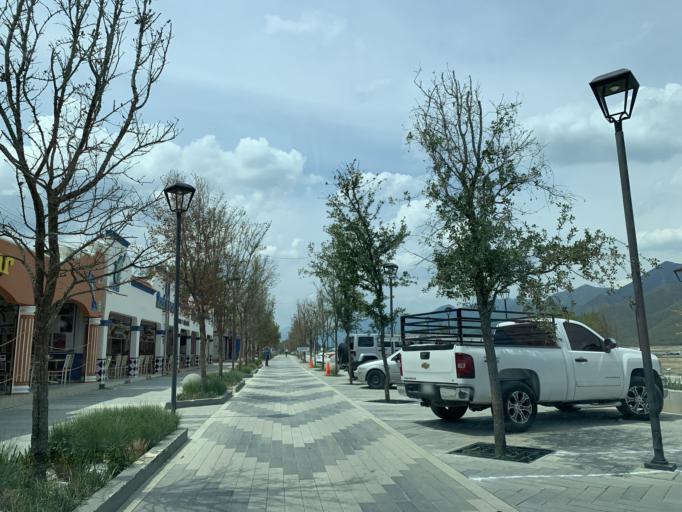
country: MX
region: Nuevo Leon
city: Santiago
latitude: 25.4130
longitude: -100.1388
